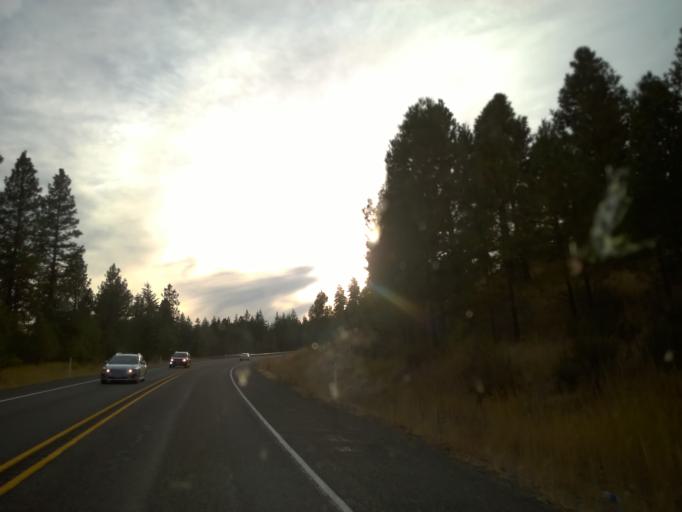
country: US
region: Washington
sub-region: Kittitas County
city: Cle Elum
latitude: 47.1995
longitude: -120.7178
